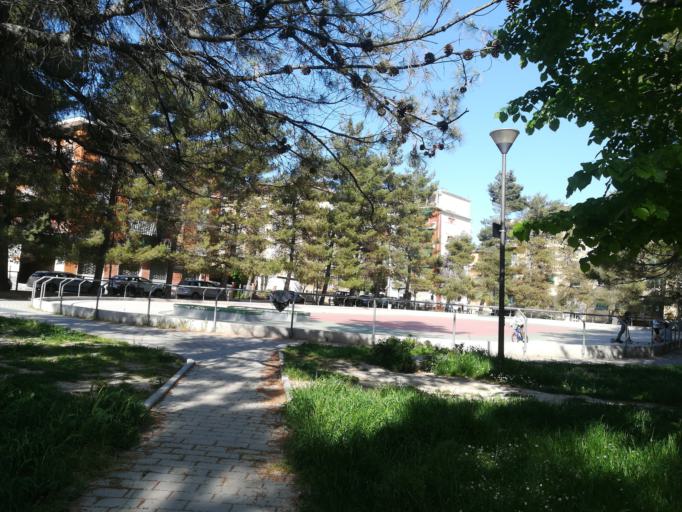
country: IT
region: The Marches
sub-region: Provincia di Macerata
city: Macerata
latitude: 43.2953
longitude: 13.4353
